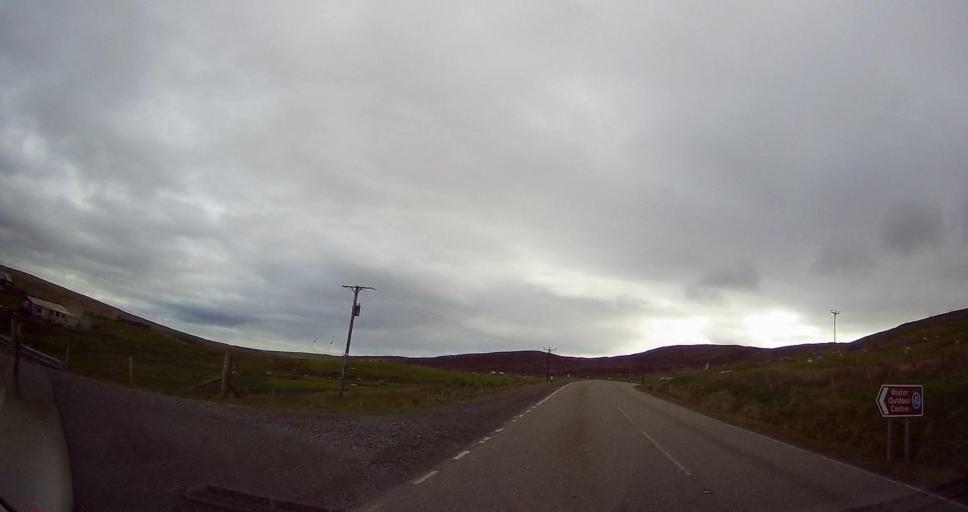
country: GB
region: Scotland
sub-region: Shetland Islands
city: Lerwick
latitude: 60.4106
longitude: -1.3278
